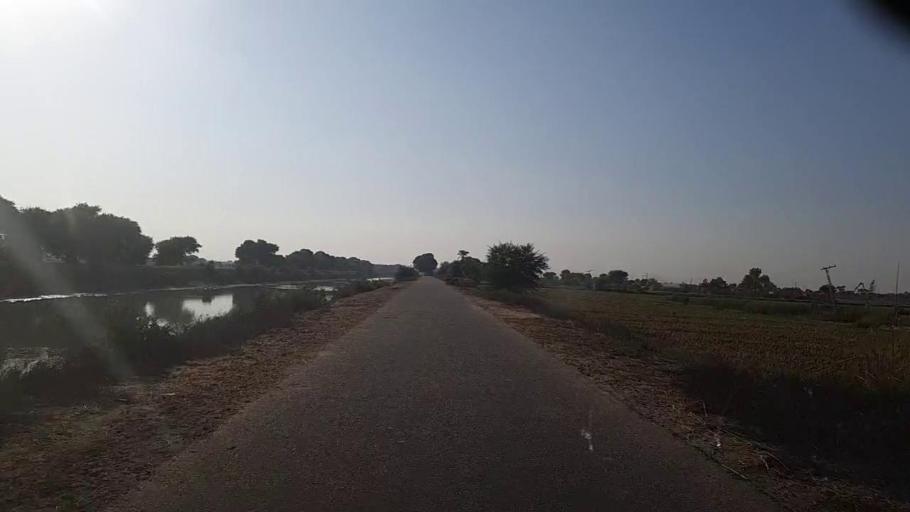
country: PK
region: Sindh
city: Tangwani
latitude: 28.3013
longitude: 68.9369
